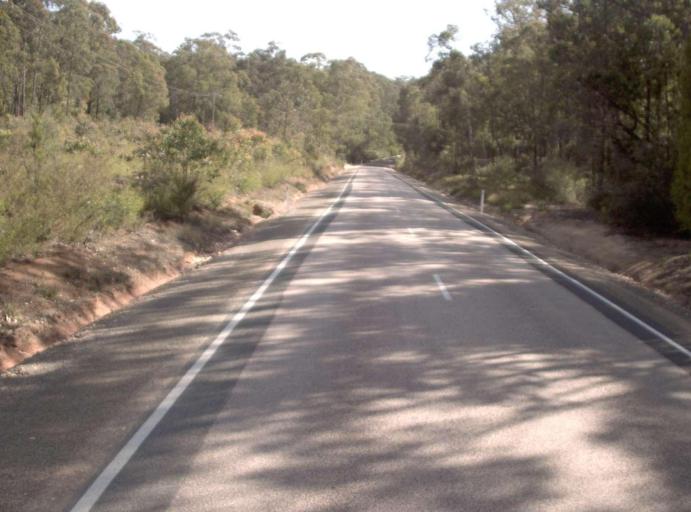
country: AU
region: Victoria
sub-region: East Gippsland
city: Lakes Entrance
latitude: -37.6722
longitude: 148.0578
